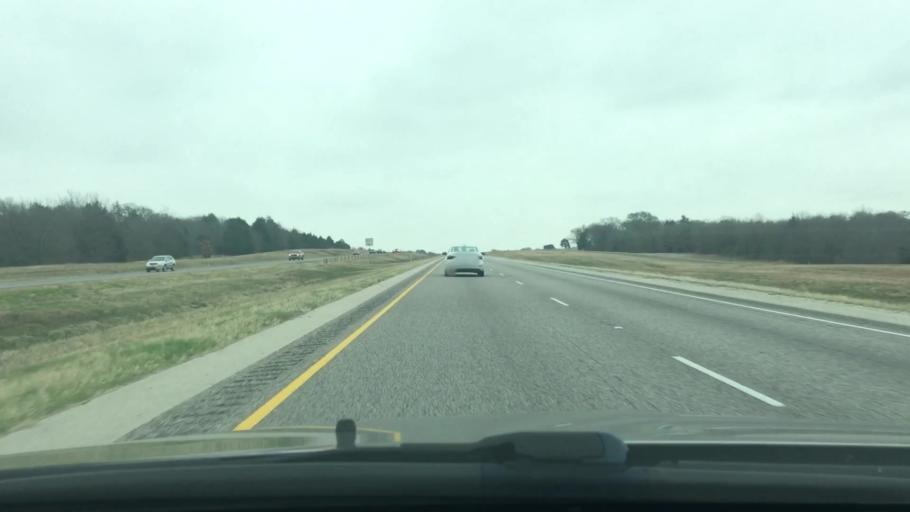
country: US
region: Texas
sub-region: Freestone County
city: Fairfield
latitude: 31.7876
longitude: -96.2433
